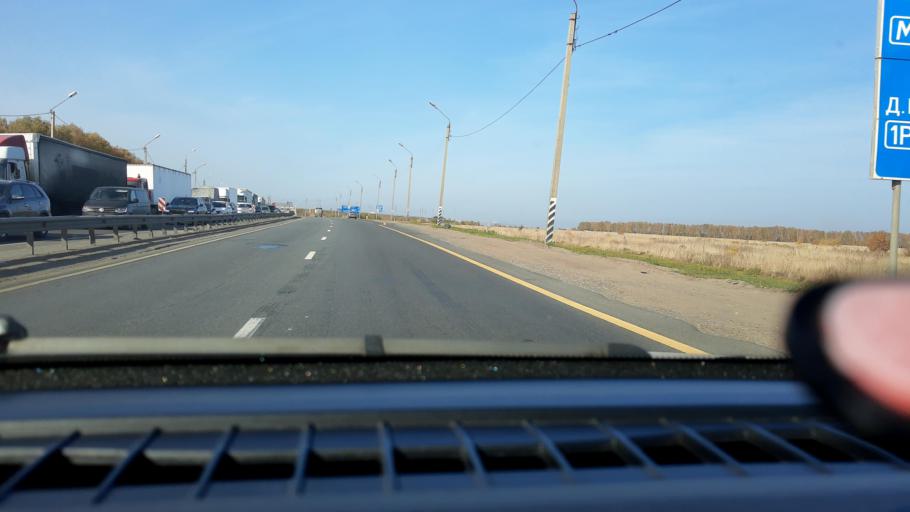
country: RU
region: Nizjnij Novgorod
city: Kstovo
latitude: 56.1244
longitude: 44.2675
